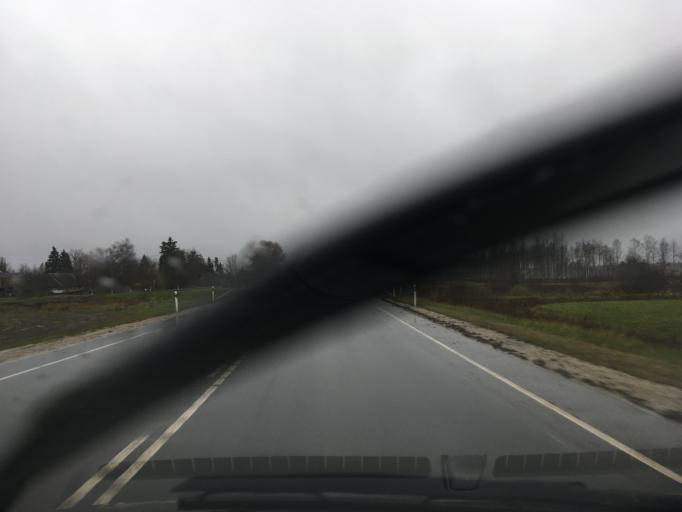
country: EE
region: Harju
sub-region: Nissi vald
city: Turba
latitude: 58.8616
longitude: 24.0748
